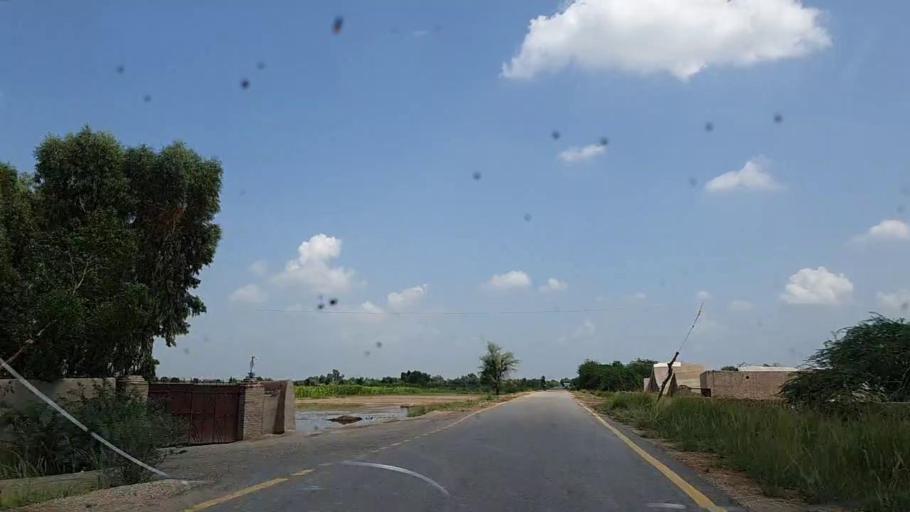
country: PK
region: Sindh
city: Tharu Shah
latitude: 26.9722
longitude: 68.0900
